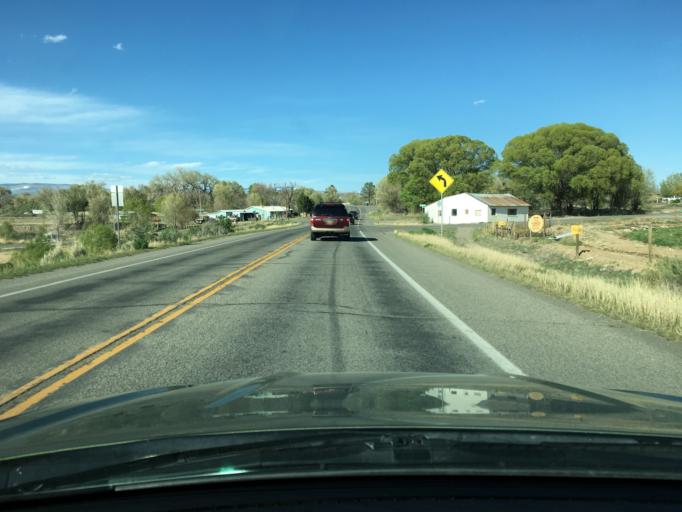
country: US
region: Colorado
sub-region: Delta County
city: Orchard City
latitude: 38.7876
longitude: -107.9913
